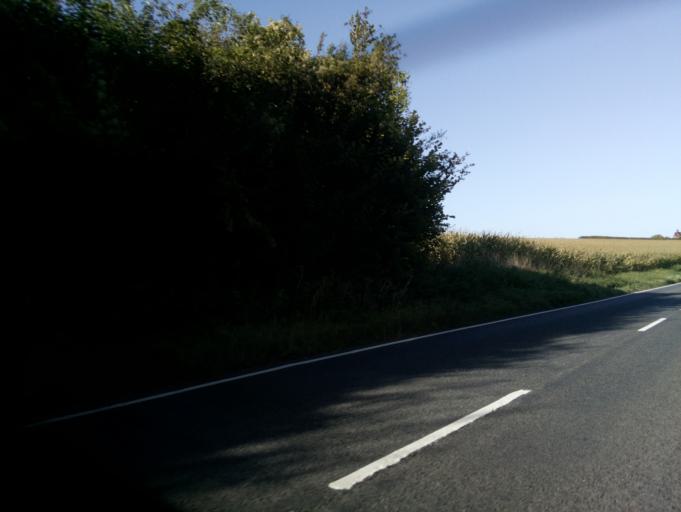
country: GB
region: England
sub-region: Hampshire
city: Swanmore
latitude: 50.9328
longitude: -1.1448
